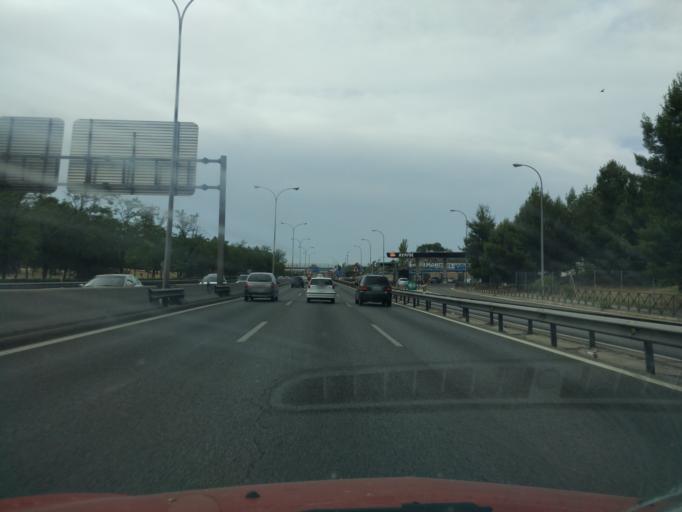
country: ES
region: Madrid
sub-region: Provincia de Madrid
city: Carabanchel
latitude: 40.3775
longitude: -3.7191
